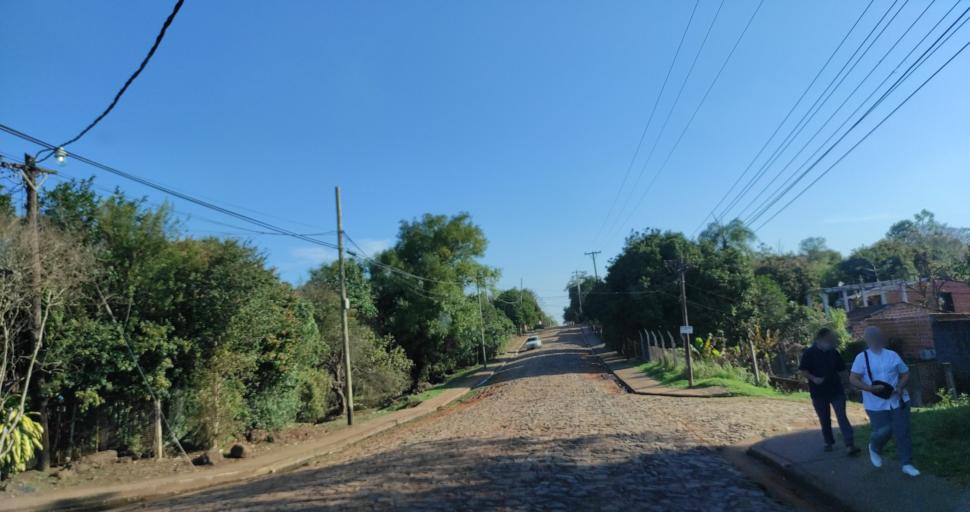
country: AR
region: Misiones
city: Garupa
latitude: -27.4489
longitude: -55.8615
